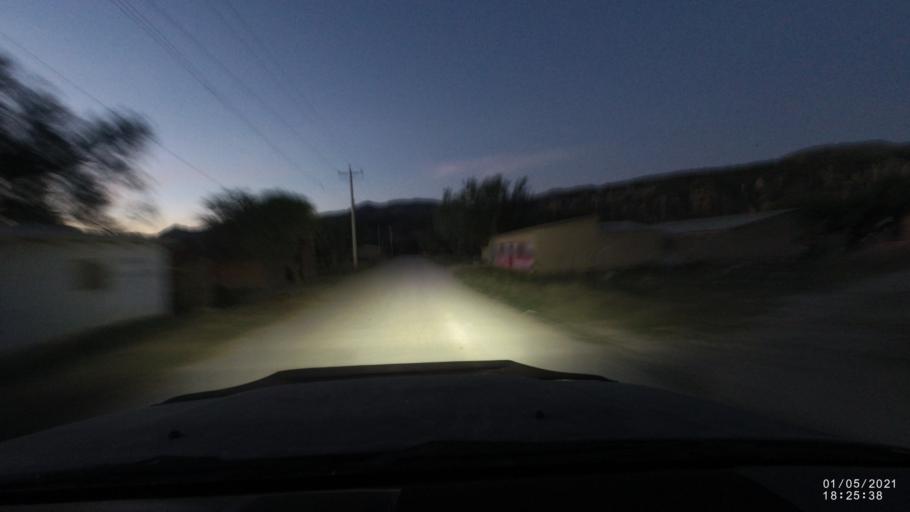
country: BO
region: Cochabamba
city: Capinota
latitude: -17.6542
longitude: -66.2418
